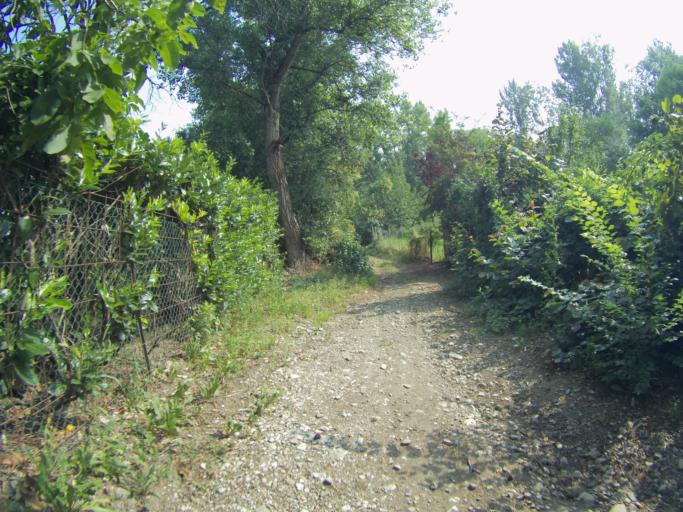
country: IT
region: Emilia-Romagna
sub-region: Provincia di Reggio Emilia
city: Pratissolo
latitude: 44.5884
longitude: 10.6717
